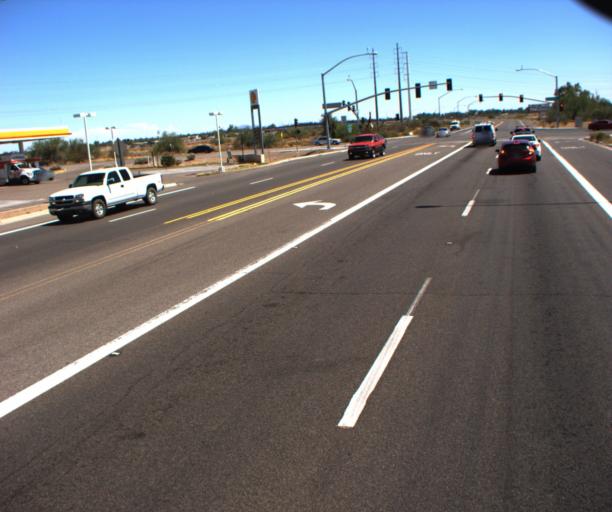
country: US
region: Arizona
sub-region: Maricopa County
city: Mesa
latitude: 33.4668
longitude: -111.8433
